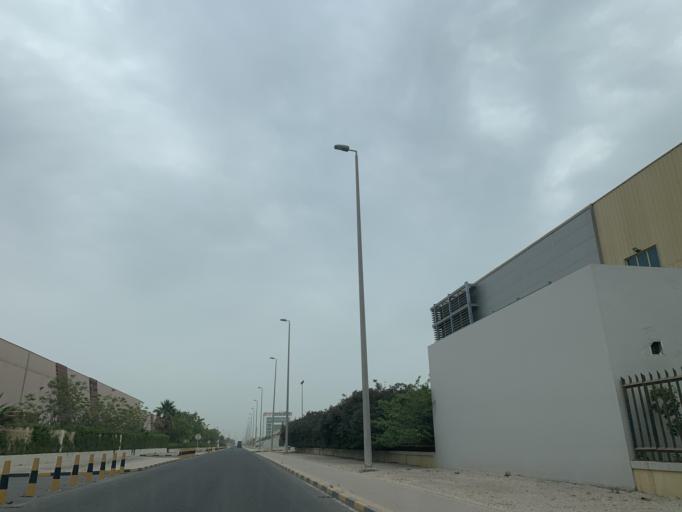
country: BH
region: Muharraq
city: Al Hadd
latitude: 26.2232
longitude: 50.6683
